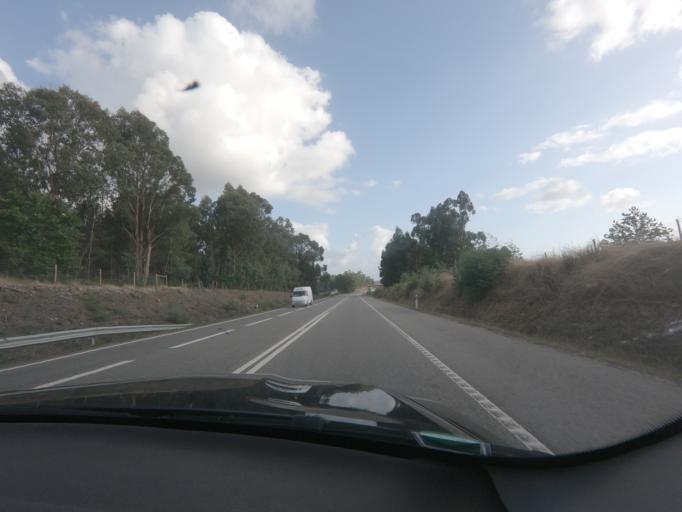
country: PT
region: Viseu
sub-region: Concelho de Tondela
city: Tondela
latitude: 40.5535
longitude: -8.0524
